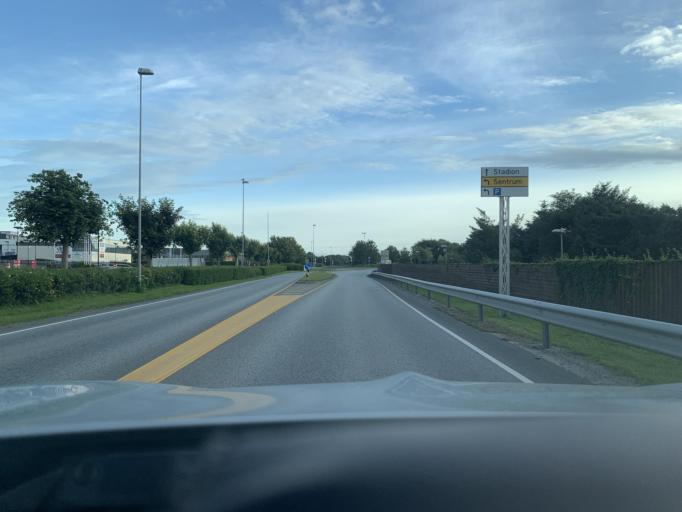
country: NO
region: Rogaland
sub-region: Time
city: Bryne
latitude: 58.7367
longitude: 5.6389
